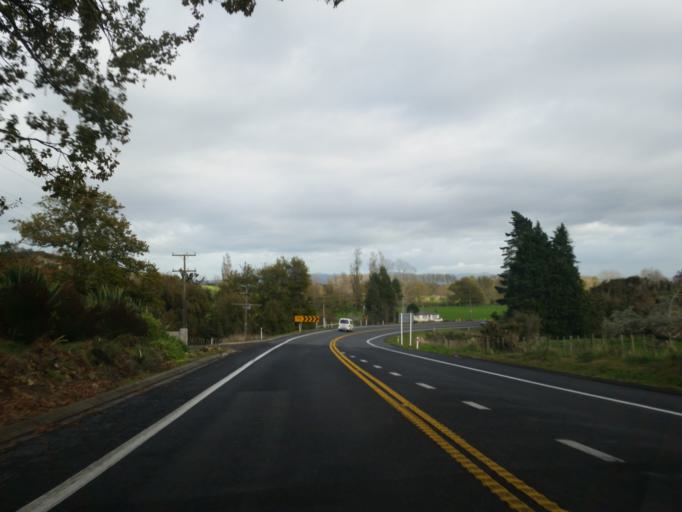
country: NZ
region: Waikato
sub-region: Hauraki District
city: Paeroa
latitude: -37.4026
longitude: 175.7018
